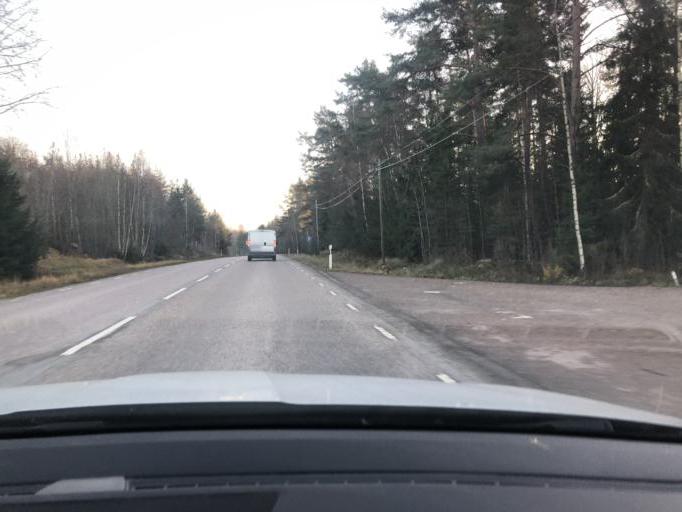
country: SE
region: Soedermanland
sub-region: Strangnas Kommun
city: Akers Styckebruk
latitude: 59.2986
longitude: 17.1002
